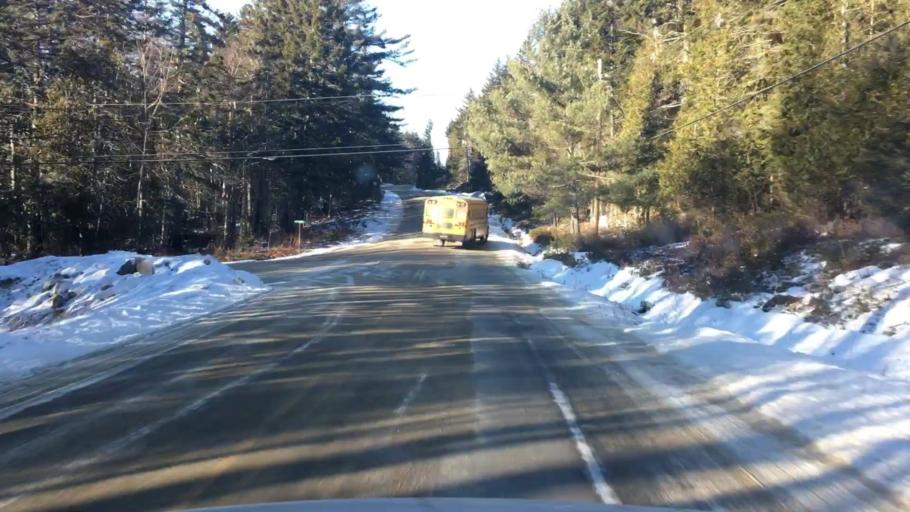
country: US
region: Maine
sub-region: Hancock County
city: Castine
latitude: 44.3596
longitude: -68.7498
